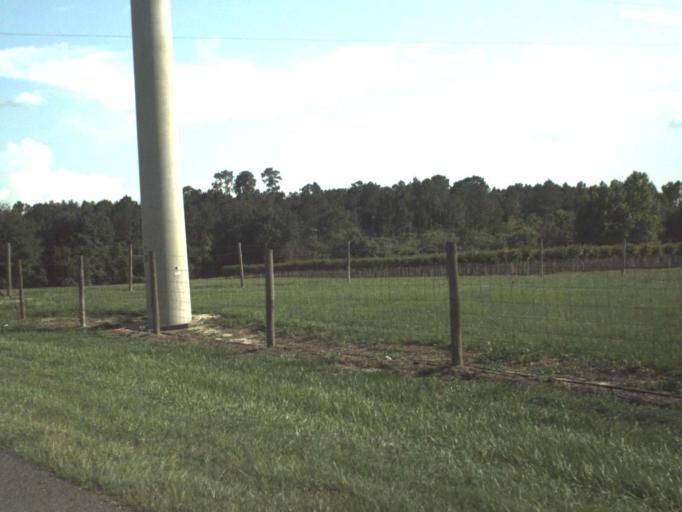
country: US
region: Florida
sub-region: Lake County
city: Groveland
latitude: 28.5220
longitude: -81.8448
